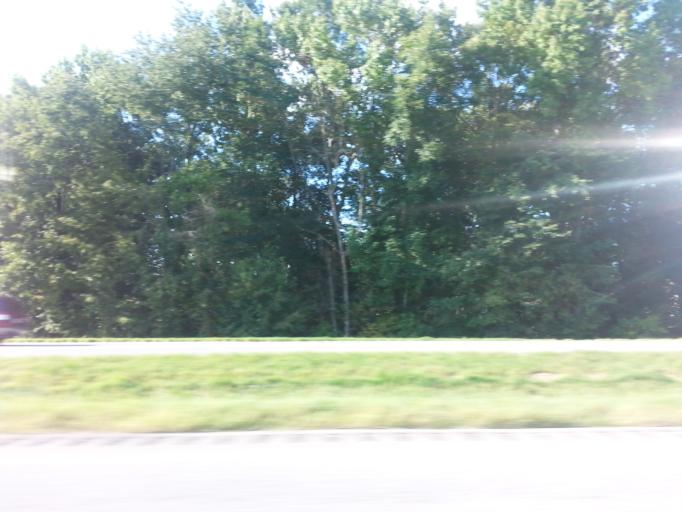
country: US
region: Alabama
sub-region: Colbert County
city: Tuscumbia
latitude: 34.7122
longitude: -87.7192
